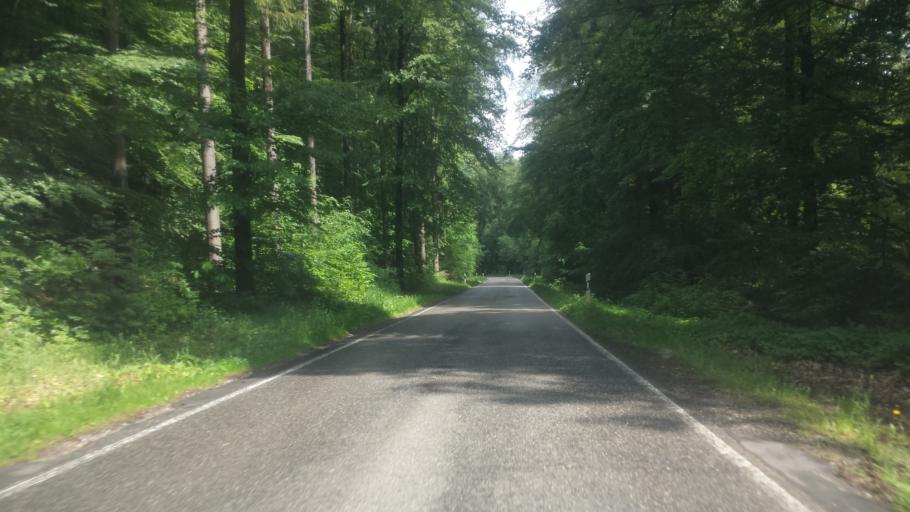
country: DE
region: Rheinland-Pfalz
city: Lindenberg
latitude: 49.4150
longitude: 8.1113
